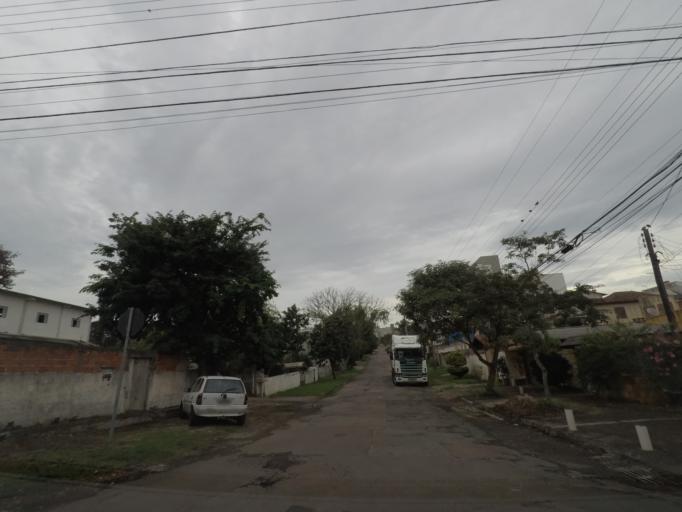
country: BR
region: Parana
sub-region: Curitiba
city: Curitiba
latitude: -25.4687
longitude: -49.3018
